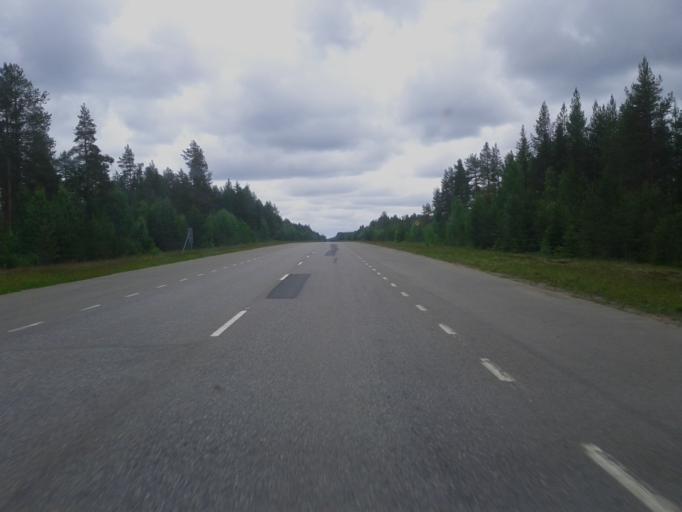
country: SE
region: Vaesterbotten
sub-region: Skelleftea Kommun
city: Storvik
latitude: 65.0891
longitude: 20.7782
